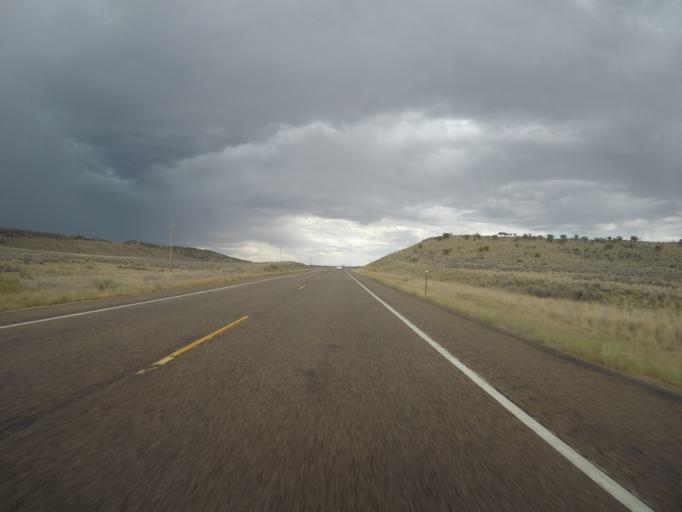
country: US
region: Colorado
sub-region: Rio Blanco County
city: Rangely
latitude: 40.2409
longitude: -108.9331
